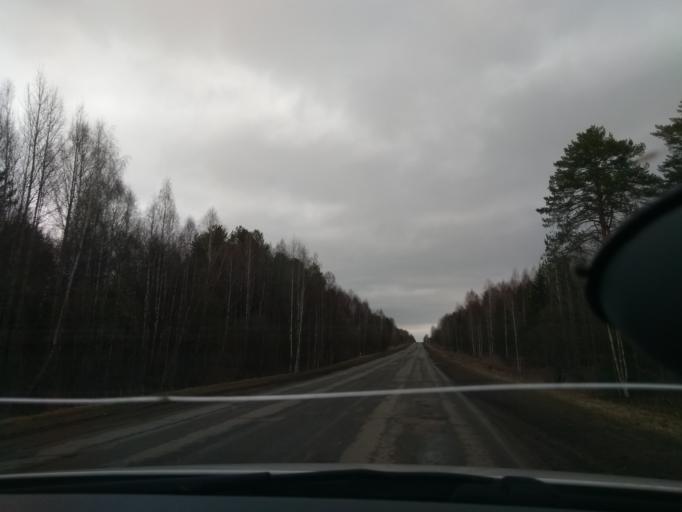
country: RU
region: Perm
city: Kungur
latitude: 57.3610
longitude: 56.8169
